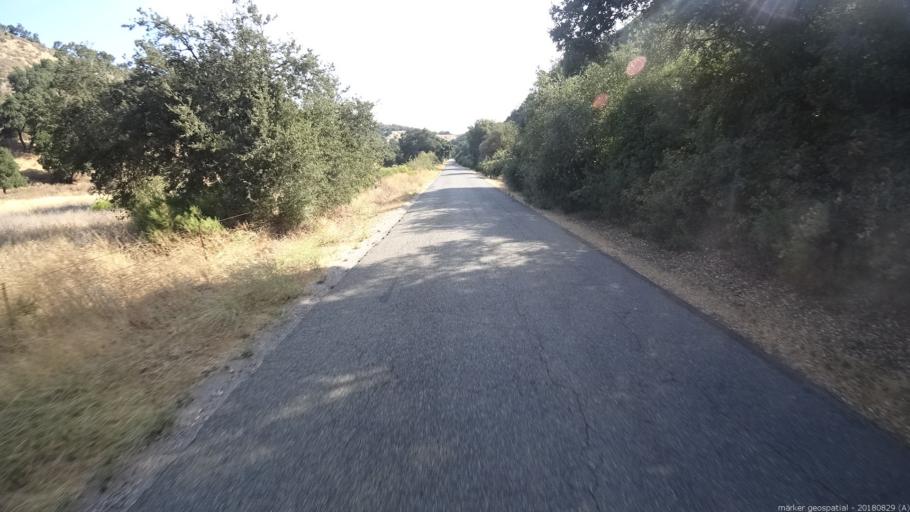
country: US
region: California
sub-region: Monterey County
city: King City
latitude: 36.0407
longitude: -121.0790
